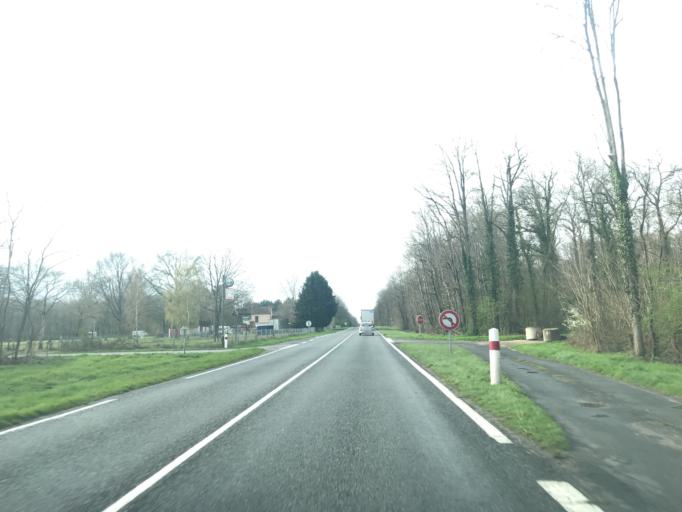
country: FR
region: Centre
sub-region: Departement du Loiret
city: Nevoy
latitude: 47.7309
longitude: 2.5745
